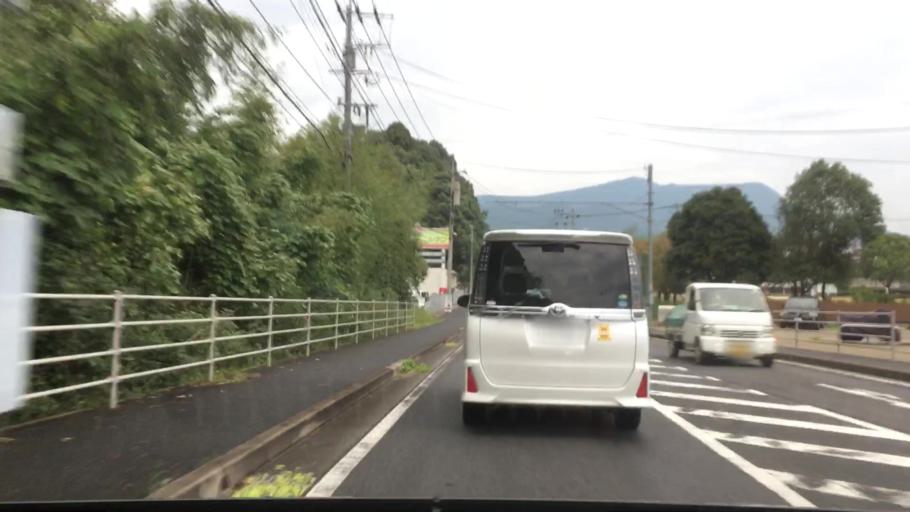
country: JP
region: Nagasaki
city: Sasebo
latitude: 33.1269
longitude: 129.7922
